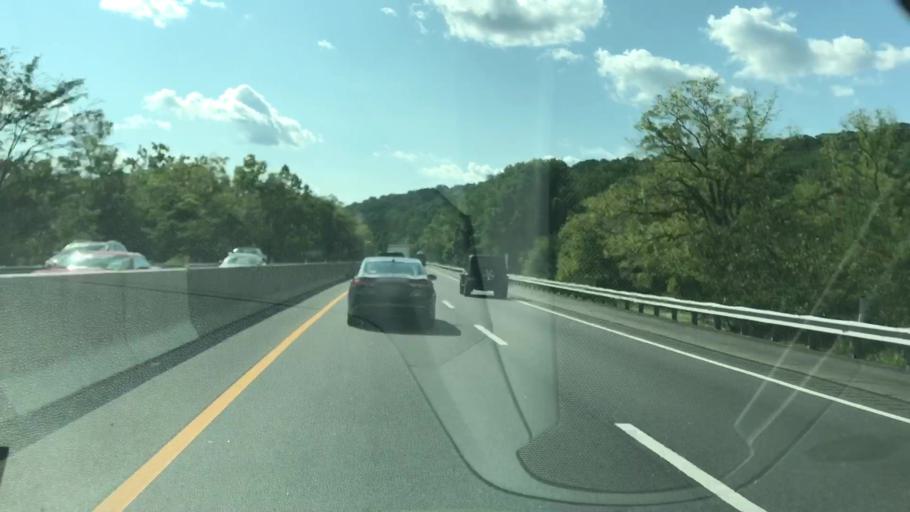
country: US
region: Pennsylvania
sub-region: Chester County
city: Chesterbrook
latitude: 40.0761
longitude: -75.4929
